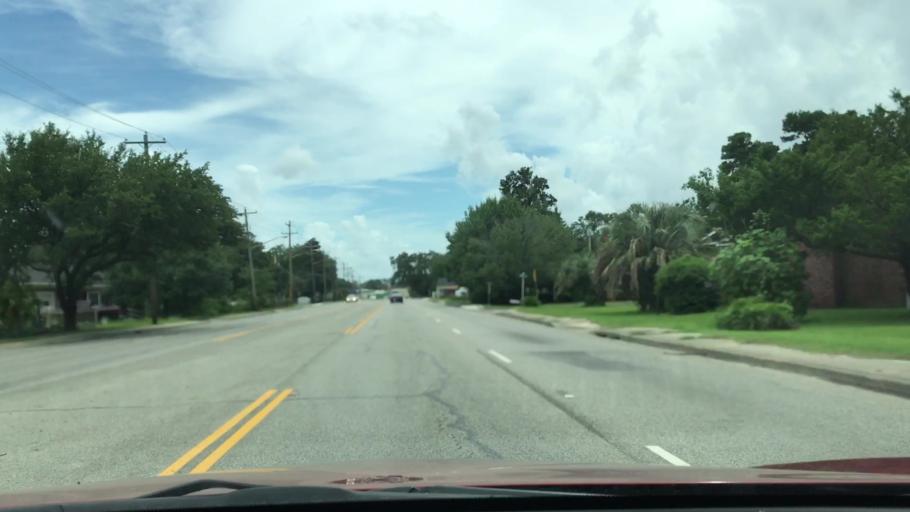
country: US
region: South Carolina
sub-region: Georgetown County
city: Georgetown
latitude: 33.3786
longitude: -79.2877
